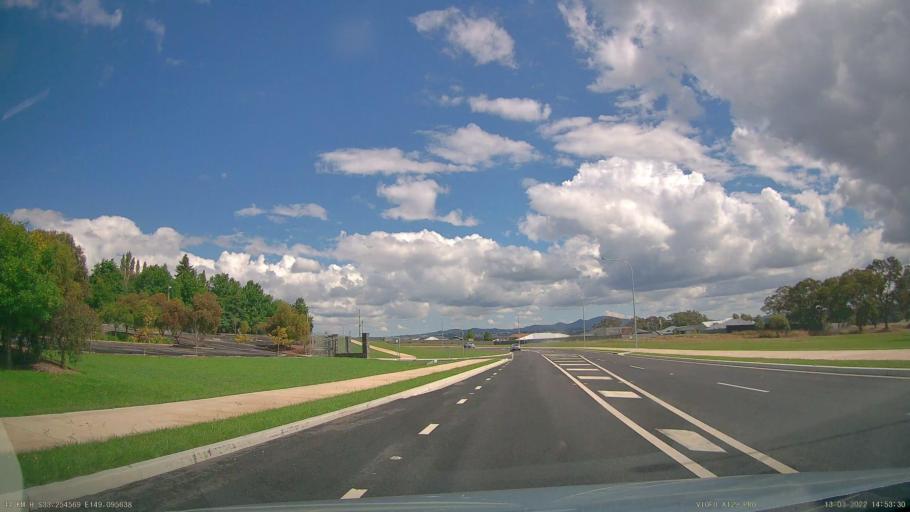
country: AU
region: New South Wales
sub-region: Orange Municipality
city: Orange
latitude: -33.2547
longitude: 149.0956
